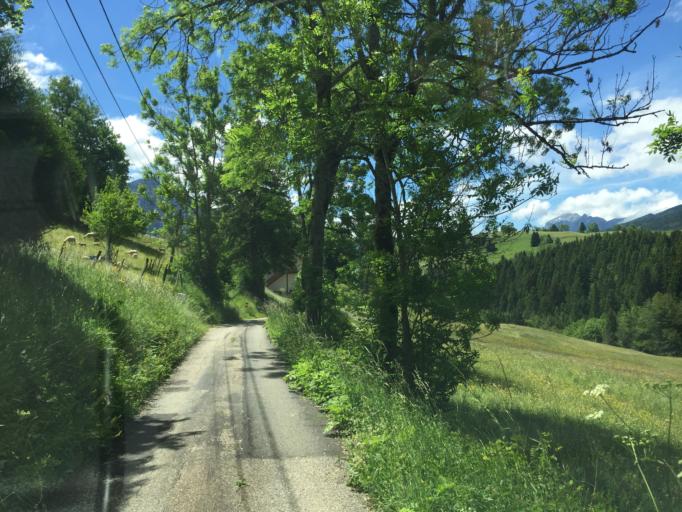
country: FR
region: Rhone-Alpes
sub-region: Departement de la Savoie
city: Vimines
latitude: 45.4777
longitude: 5.8922
